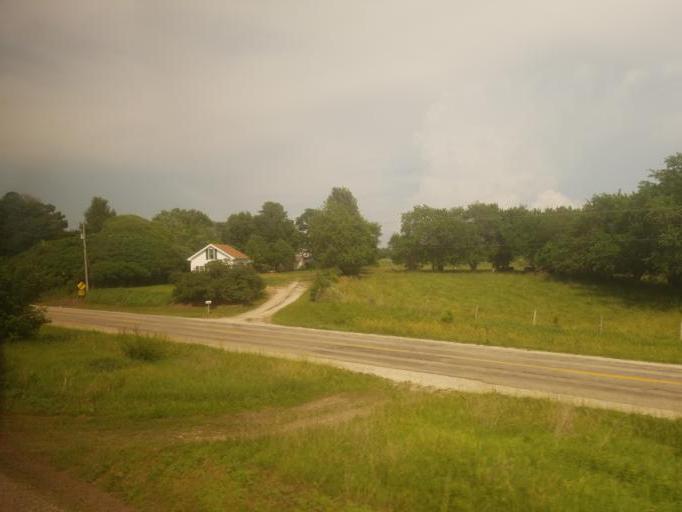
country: US
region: Illinois
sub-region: Knox County
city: Galesburg
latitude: 41.0198
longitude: -90.2873
